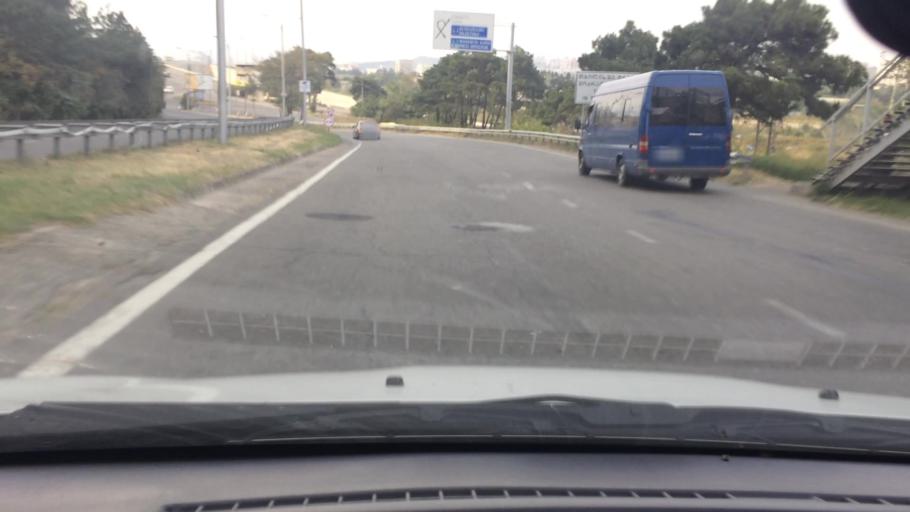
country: GE
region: T'bilisi
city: Tbilisi
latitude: 41.6591
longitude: 44.8898
